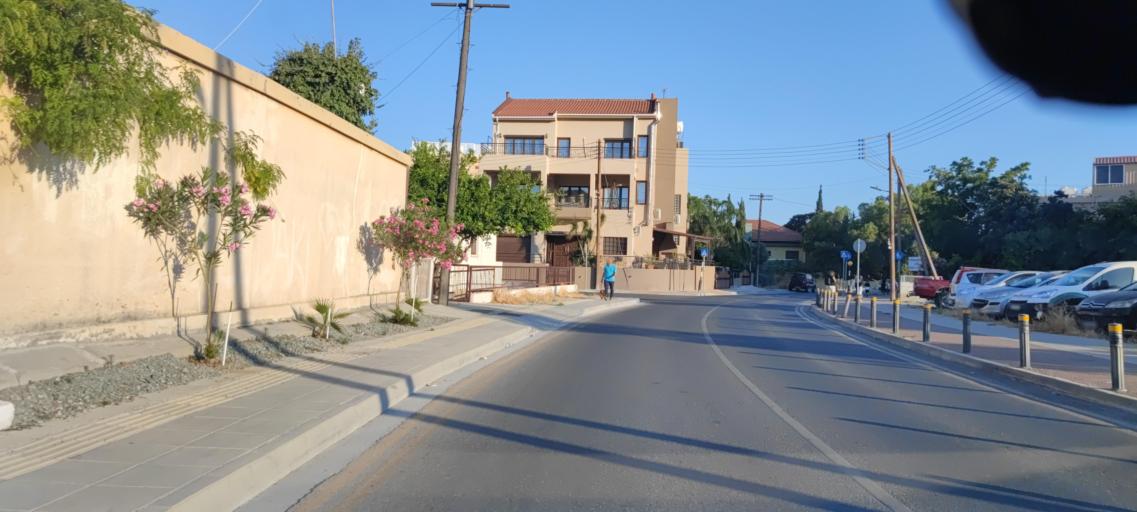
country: CY
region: Limassol
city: Limassol
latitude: 34.6778
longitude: 33.0355
